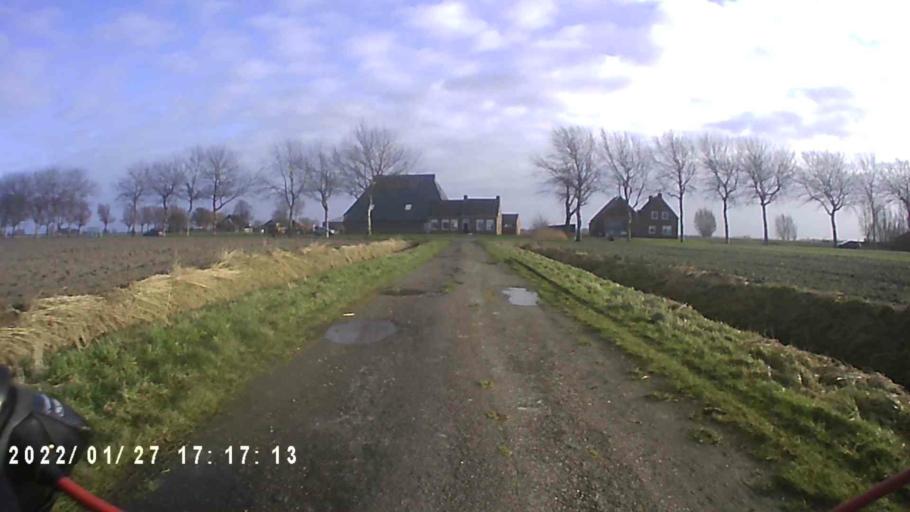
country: NL
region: Friesland
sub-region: Gemeente Dongeradeel
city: Anjum
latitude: 53.3896
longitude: 6.1009
